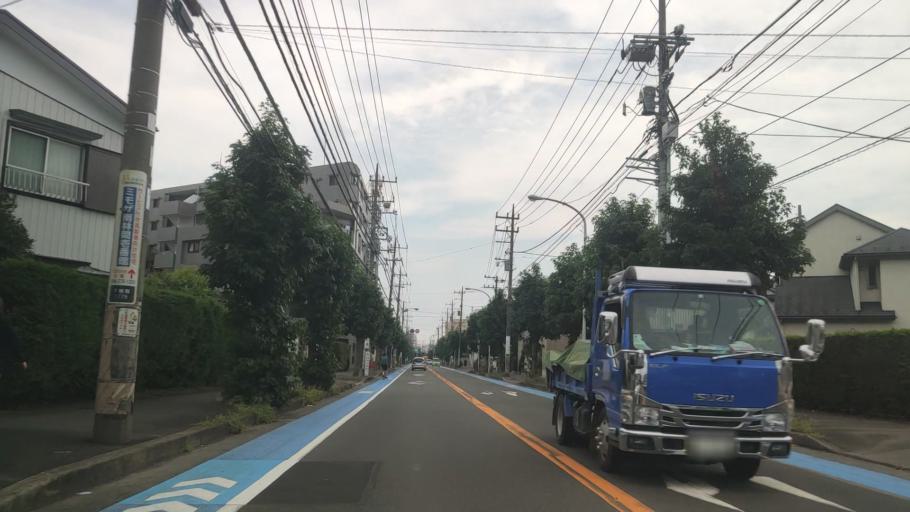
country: JP
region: Kanagawa
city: Minami-rinkan
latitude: 35.5006
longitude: 139.4503
